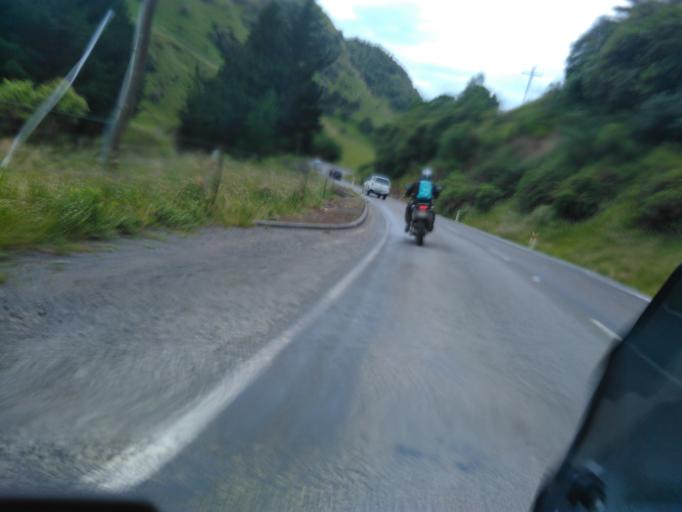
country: NZ
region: Bay of Plenty
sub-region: Opotiki District
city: Opotiki
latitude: -38.3791
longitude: 177.4788
